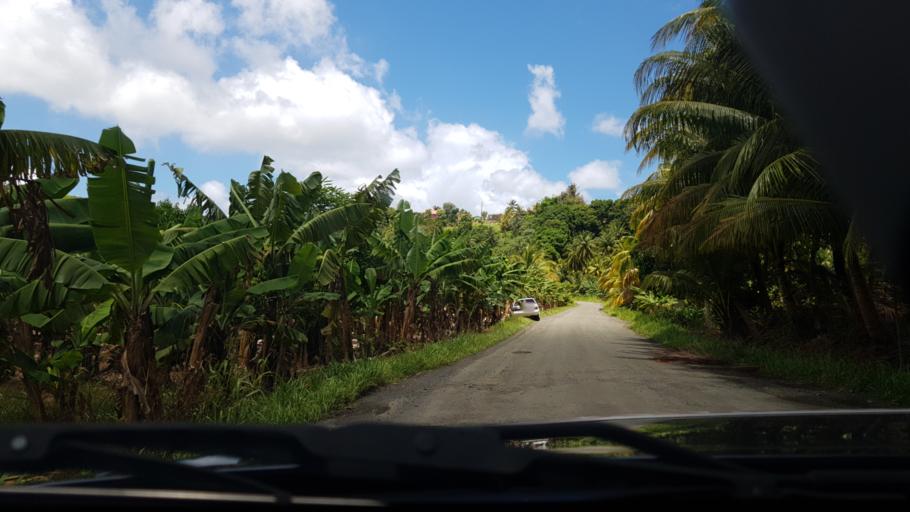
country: LC
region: Anse-la-Raye
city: Anse La Raye
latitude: 13.9526
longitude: -60.9973
